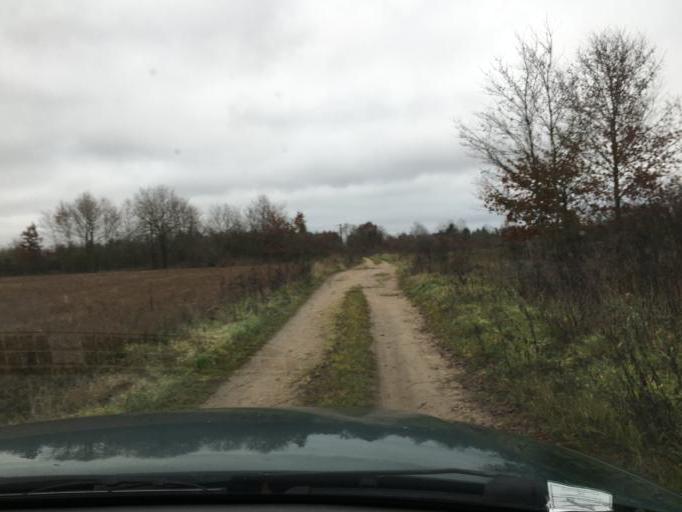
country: FR
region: Centre
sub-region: Departement du Loiret
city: Olivet
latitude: 47.8521
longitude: 1.8777
